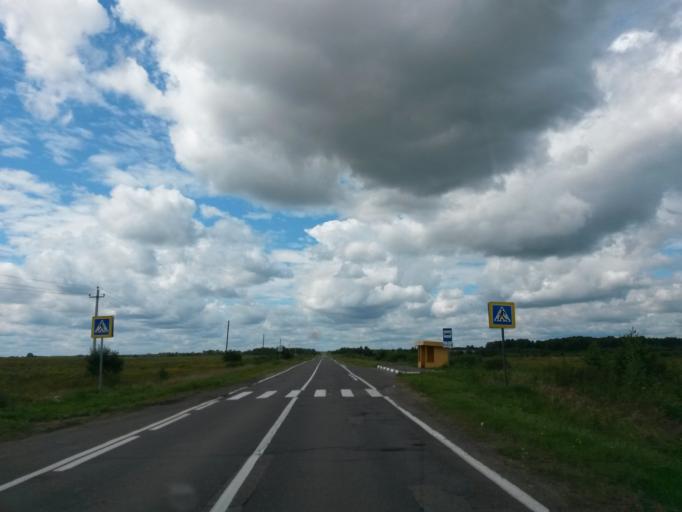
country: RU
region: Jaroslavl
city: Tutayev
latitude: 57.9477
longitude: 39.4796
